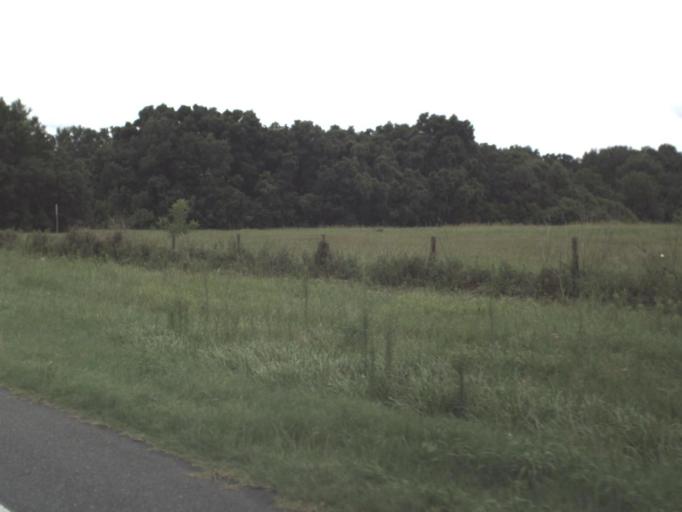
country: US
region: Florida
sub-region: Levy County
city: Williston
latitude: 29.3470
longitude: -82.4558
